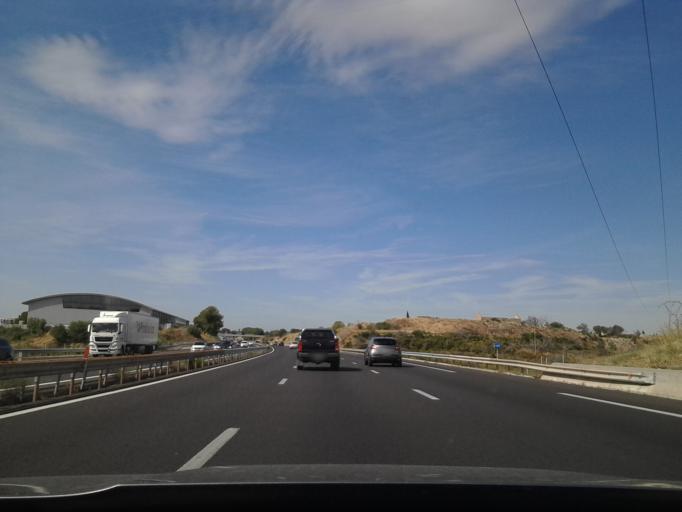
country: FR
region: Languedoc-Roussillon
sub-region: Departement de l'Herault
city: Meze
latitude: 43.4472
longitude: 3.5777
